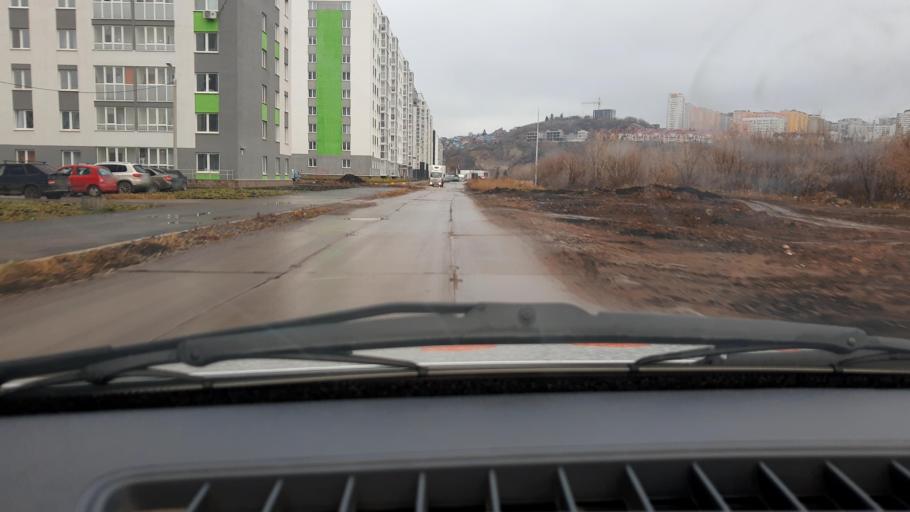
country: RU
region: Bashkortostan
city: Ufa
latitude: 54.6893
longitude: 55.9726
